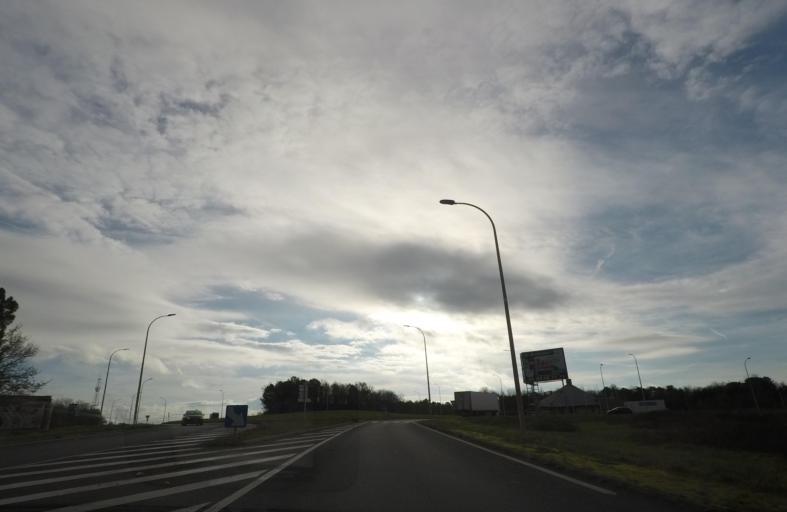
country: FR
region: Centre
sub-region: Departement du Loir-et-Cher
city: Villefranche-sur-Cher
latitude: 47.3279
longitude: 1.7609
